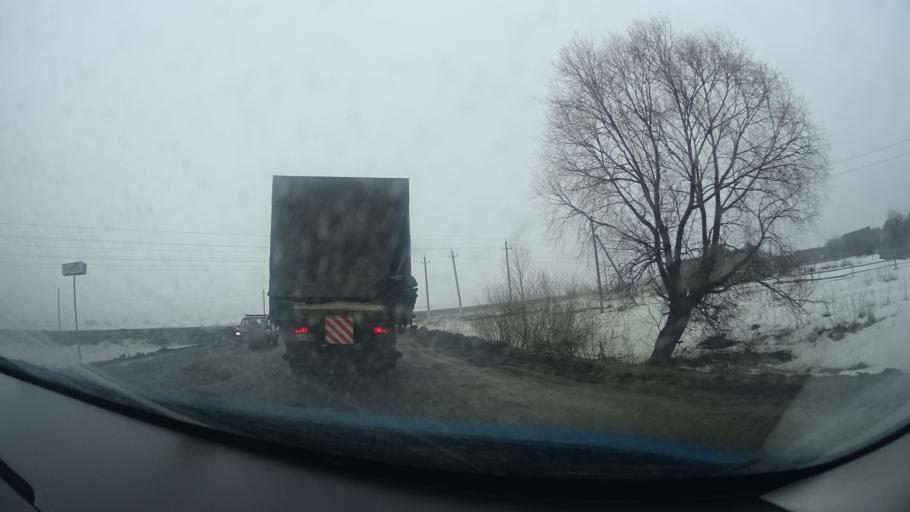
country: RU
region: Perm
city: Kuyeda
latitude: 56.4346
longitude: 55.5729
